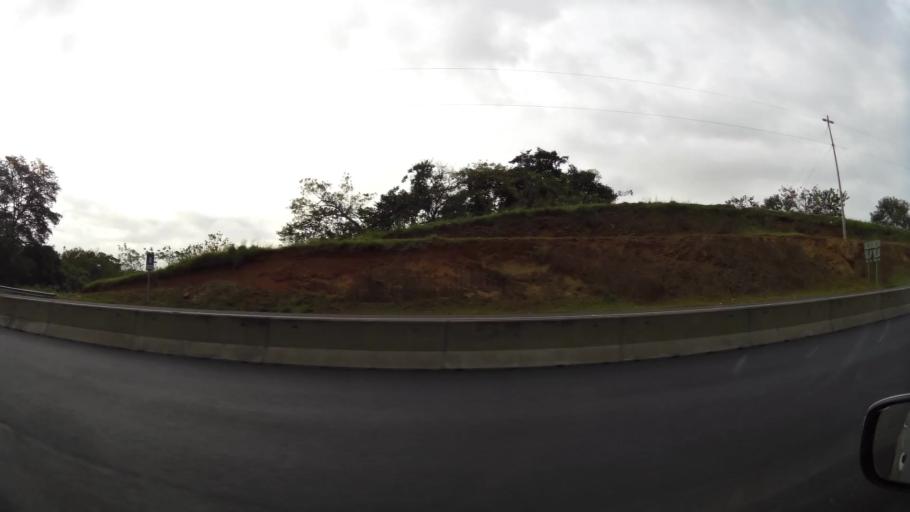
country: CR
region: Alajuela
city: Atenas
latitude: 9.9658
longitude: -84.3106
